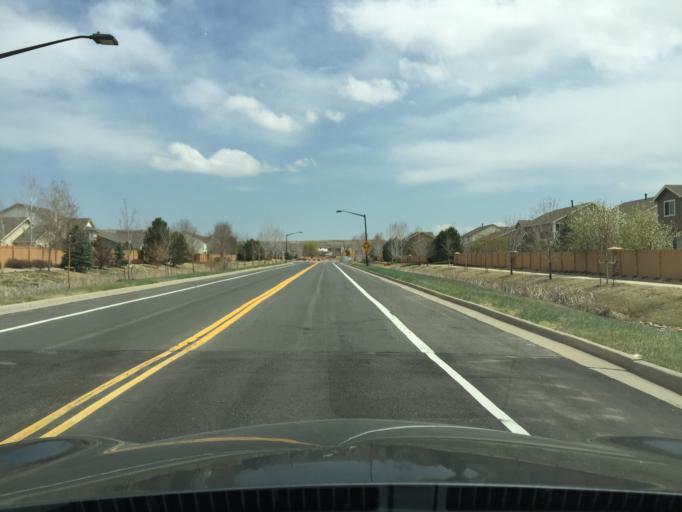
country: US
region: Colorado
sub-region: Boulder County
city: Erie
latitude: 40.0209
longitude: -105.0441
